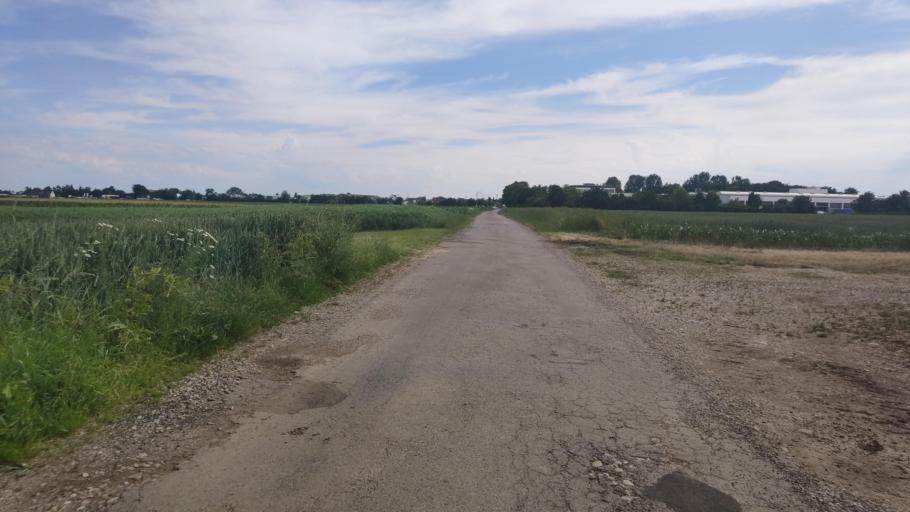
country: DE
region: Bavaria
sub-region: Swabia
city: Konigsbrunn
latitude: 48.2617
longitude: 10.8760
